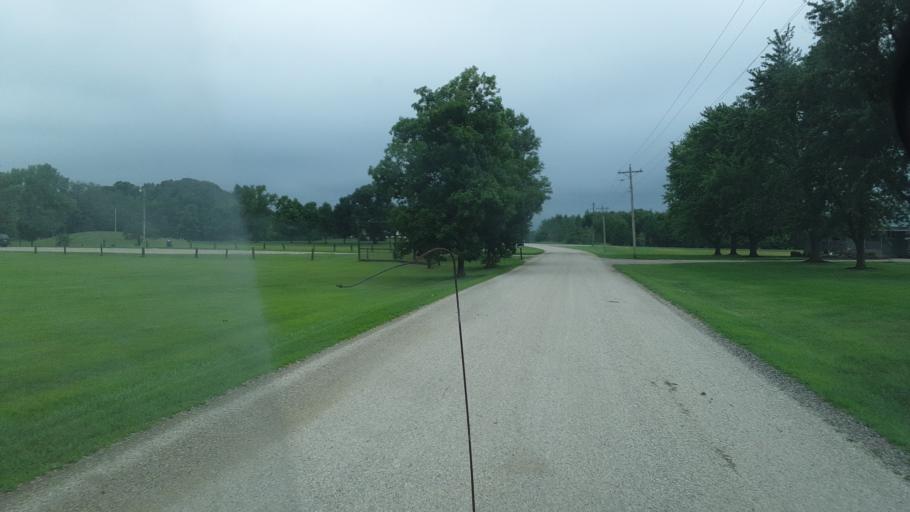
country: US
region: Indiana
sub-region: Adams County
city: Berne
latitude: 40.6424
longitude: -84.9917
